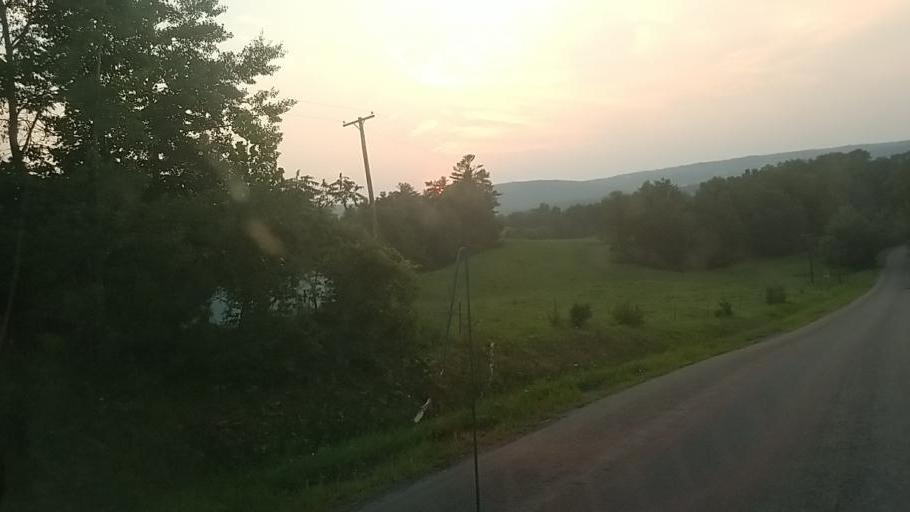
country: US
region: New York
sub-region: Montgomery County
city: Fonda
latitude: 42.9194
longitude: -74.4106
